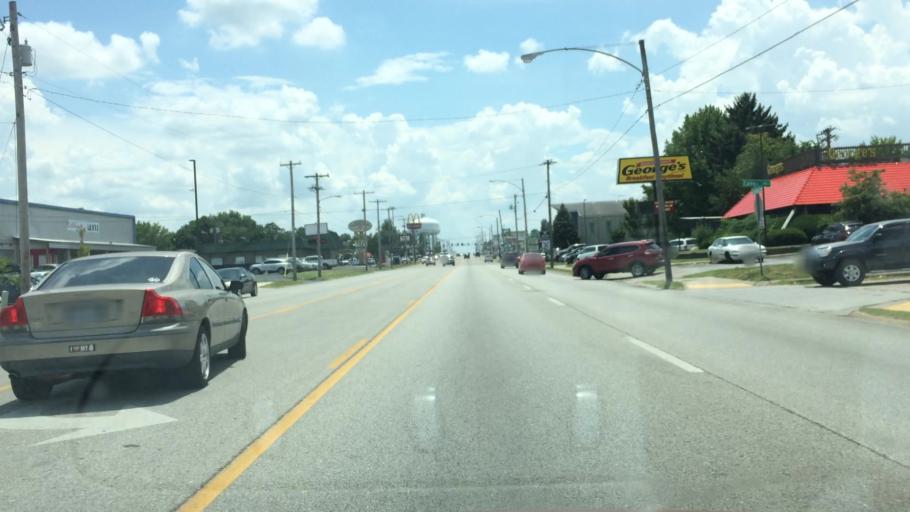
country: US
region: Missouri
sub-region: Greene County
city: Springfield
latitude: 37.2075
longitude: -93.2619
